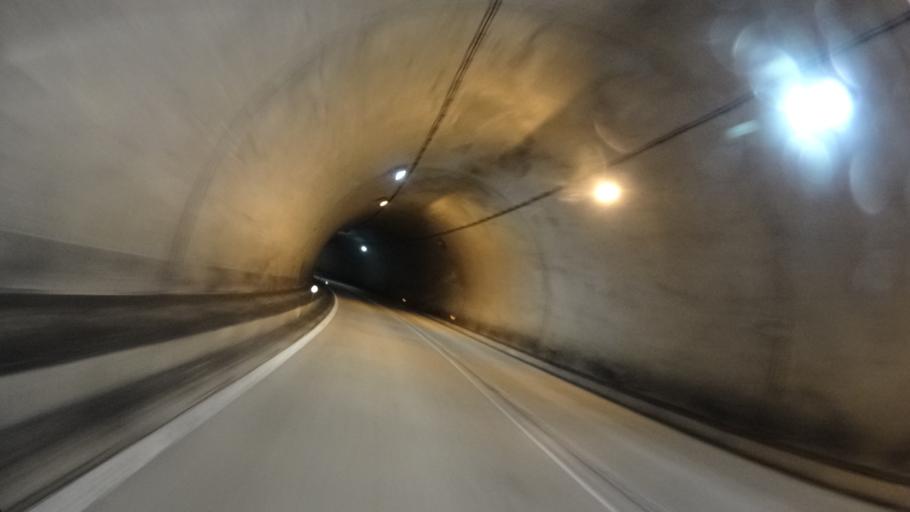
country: JP
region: Fukui
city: Maruoka
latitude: 36.1963
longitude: 136.3454
